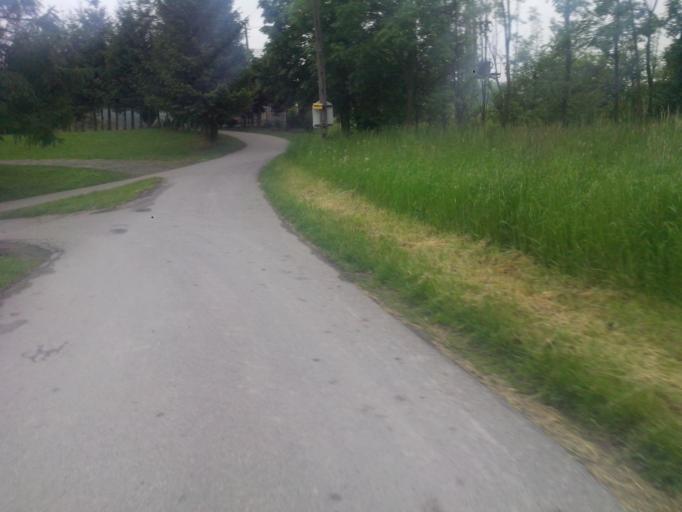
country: PL
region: Subcarpathian Voivodeship
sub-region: Powiat strzyzowski
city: Strzyzow
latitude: 49.8663
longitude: 21.8185
